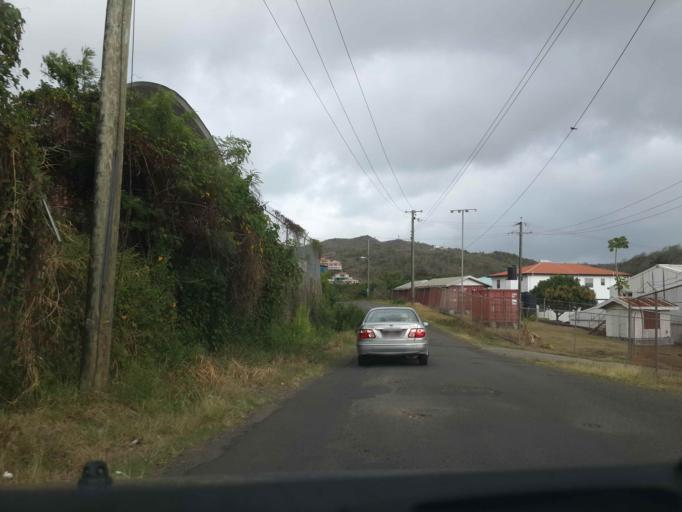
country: LC
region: Gros-Islet
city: Gros Islet
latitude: 14.0464
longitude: -60.9615
